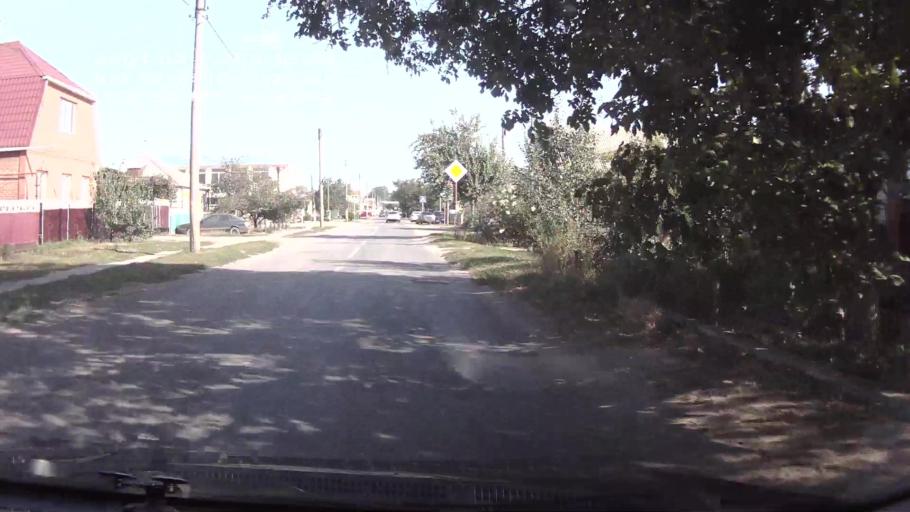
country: RU
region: Rostov
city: Tselina
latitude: 46.5339
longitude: 41.0266
